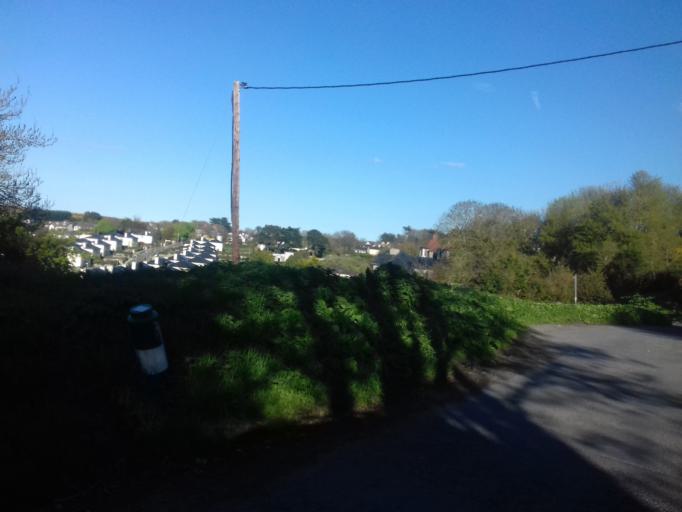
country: IE
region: Leinster
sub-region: Fingal County
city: Howth
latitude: 53.3749
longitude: -6.0611
